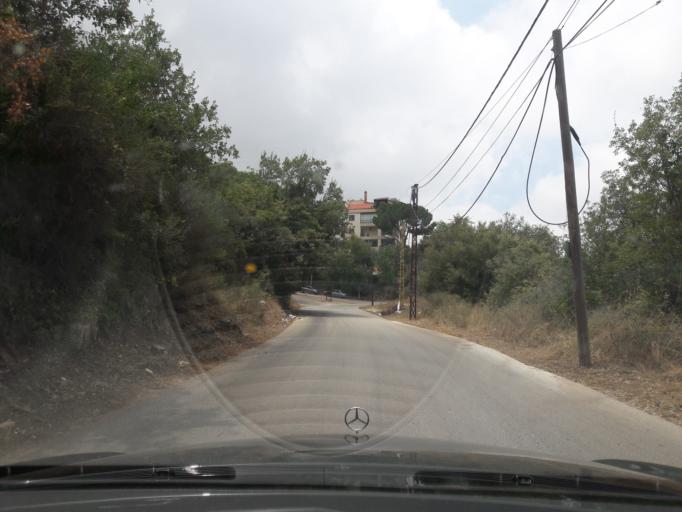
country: LB
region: Mont-Liban
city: Djounie
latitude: 33.9230
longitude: 35.6691
